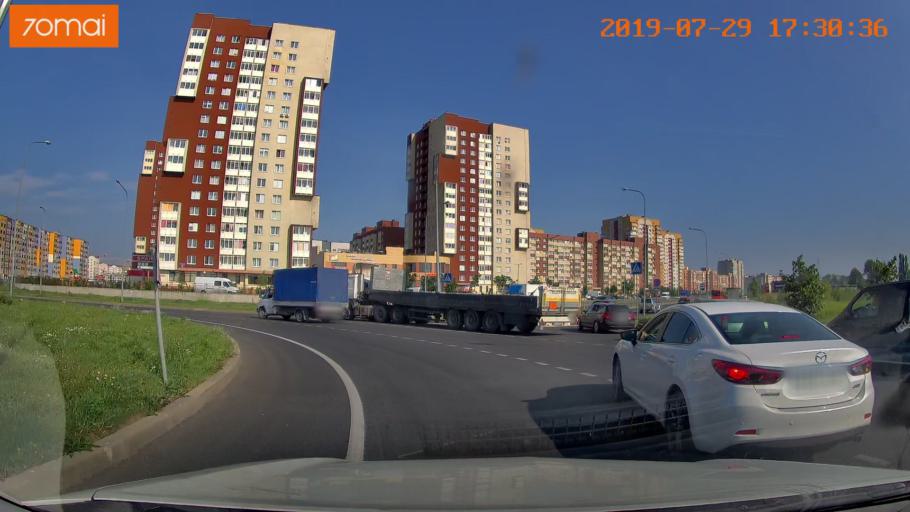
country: RU
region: Kaliningrad
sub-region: Gorod Kaliningrad
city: Kaliningrad
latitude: 54.7471
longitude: 20.4813
